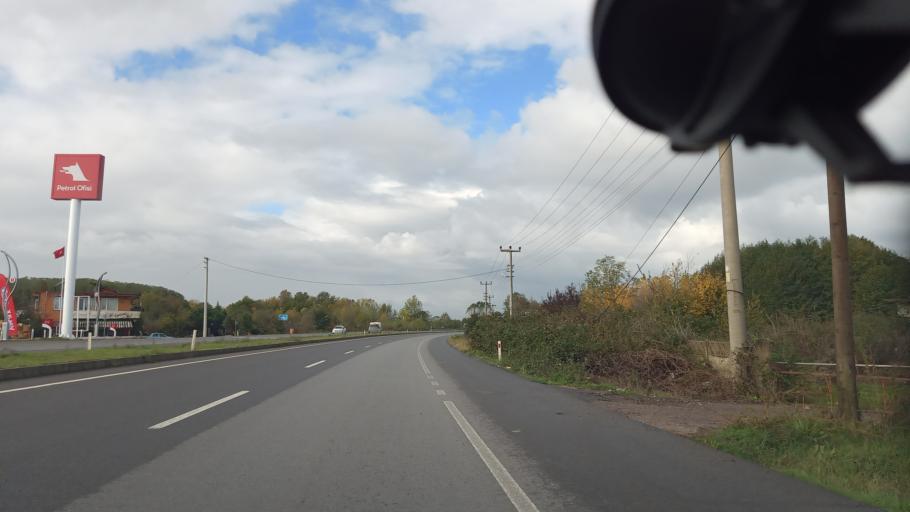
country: TR
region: Sakarya
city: Karasu
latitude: 41.0697
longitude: 30.7997
